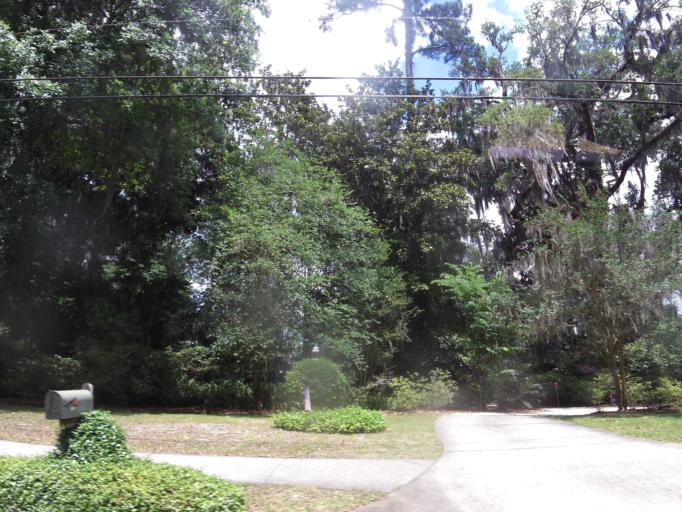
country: US
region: Florida
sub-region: Clay County
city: Orange Park
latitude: 30.1860
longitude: -81.6971
